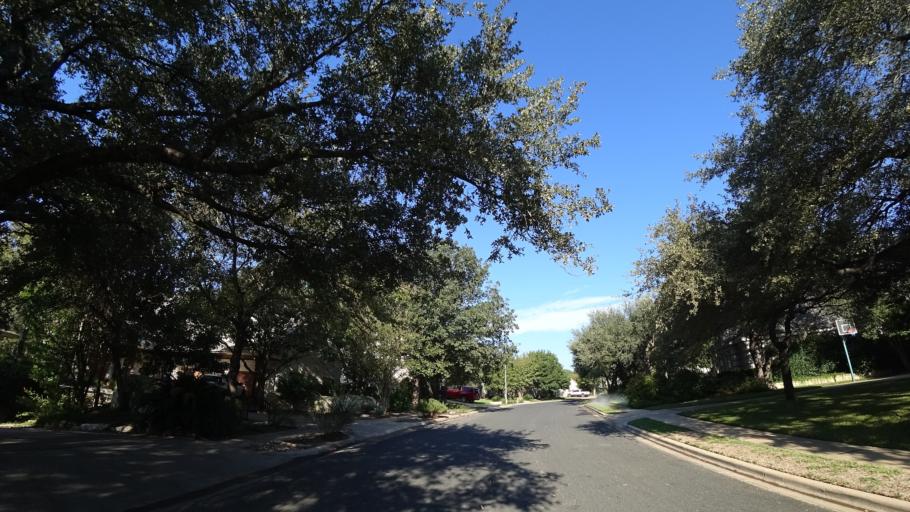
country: US
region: Texas
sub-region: Travis County
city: Rollingwood
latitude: 30.2672
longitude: -97.7957
